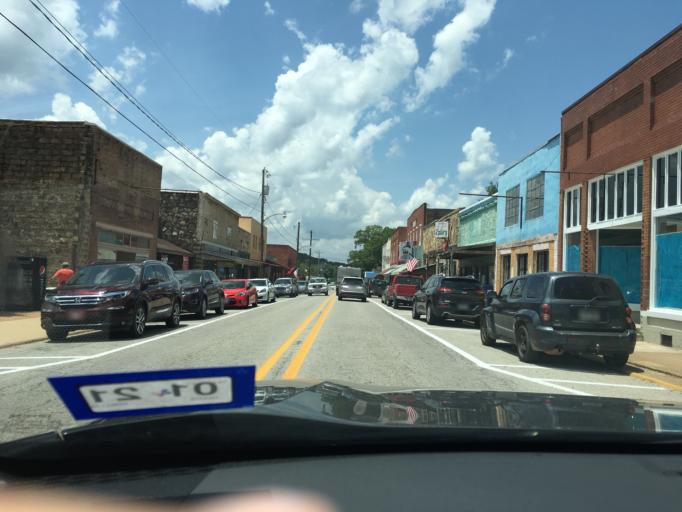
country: US
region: Arkansas
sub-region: Sharp County
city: Cherokee Village
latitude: 36.3157
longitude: -91.4813
